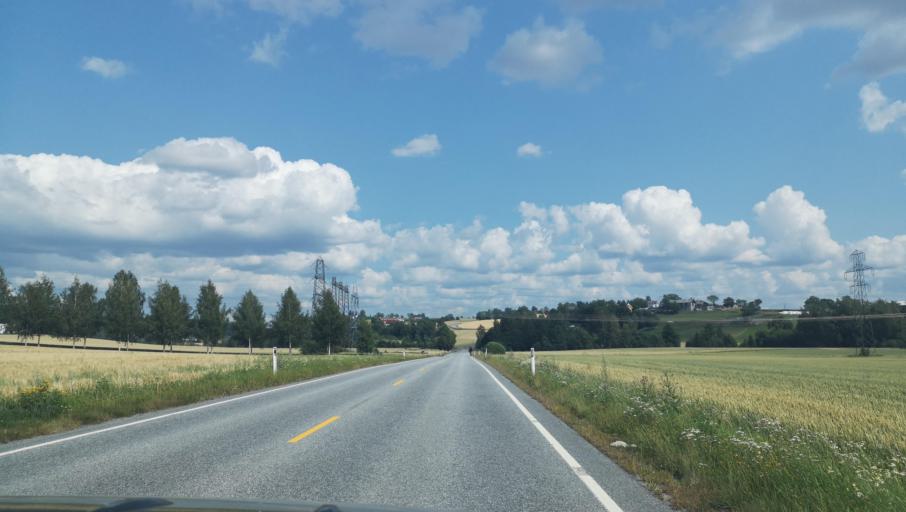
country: NO
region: Buskerud
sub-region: Ovre Eiker
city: Hokksund
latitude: 59.7219
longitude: 9.8290
